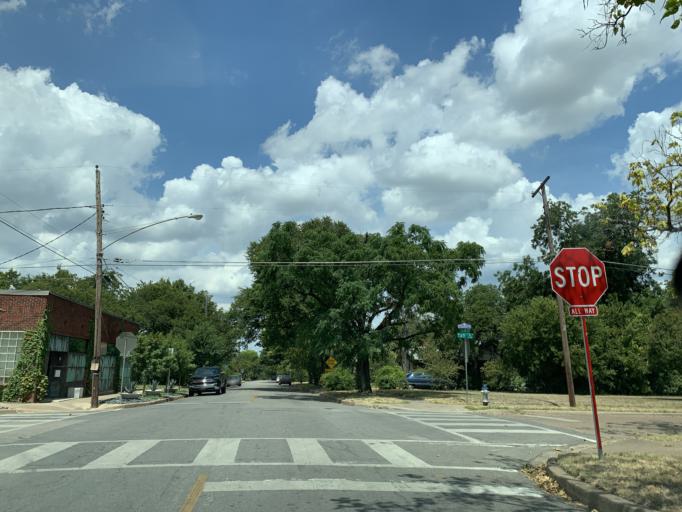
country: US
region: Texas
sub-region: Dallas County
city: Cockrell Hill
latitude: 32.7523
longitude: -96.8464
